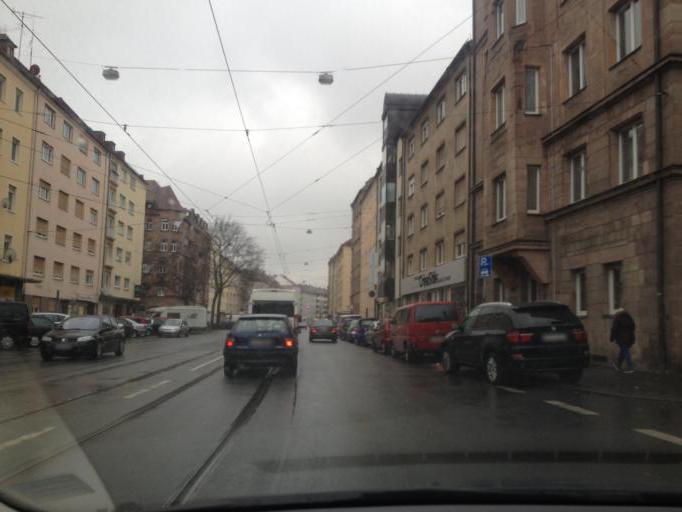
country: DE
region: Bavaria
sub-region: Regierungsbezirk Mittelfranken
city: Nuernberg
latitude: 49.4384
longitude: 11.0670
